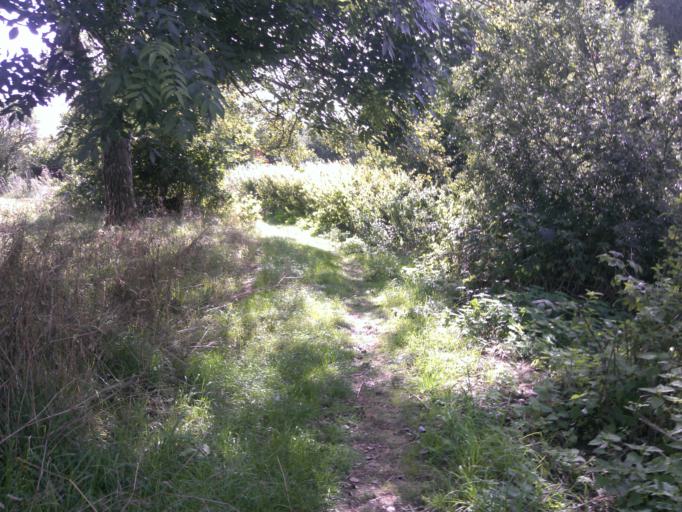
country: GB
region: England
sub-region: Essex
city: Wivenhoe
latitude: 51.8589
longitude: 0.9557
